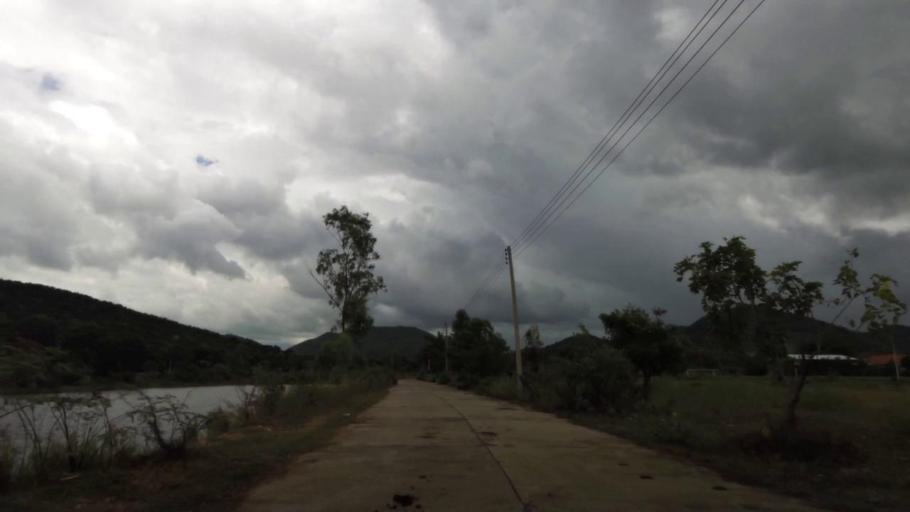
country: TH
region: Nakhon Sawan
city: Phai Sali
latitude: 15.6035
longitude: 100.6761
